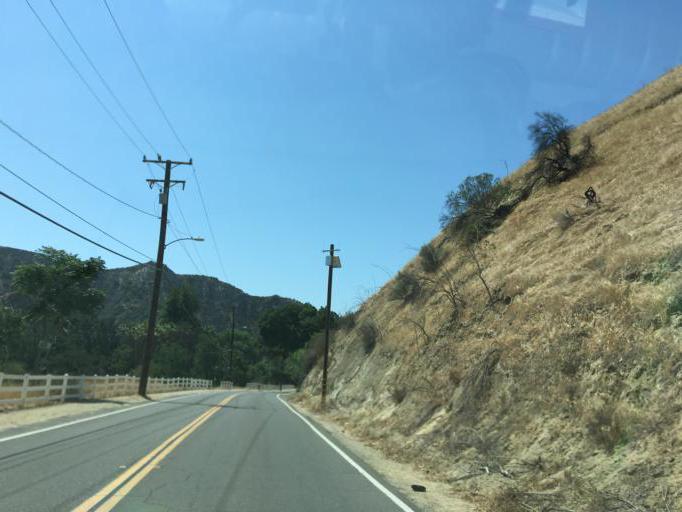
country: US
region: California
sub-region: Los Angeles County
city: Val Verde
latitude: 34.4441
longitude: -118.6576
